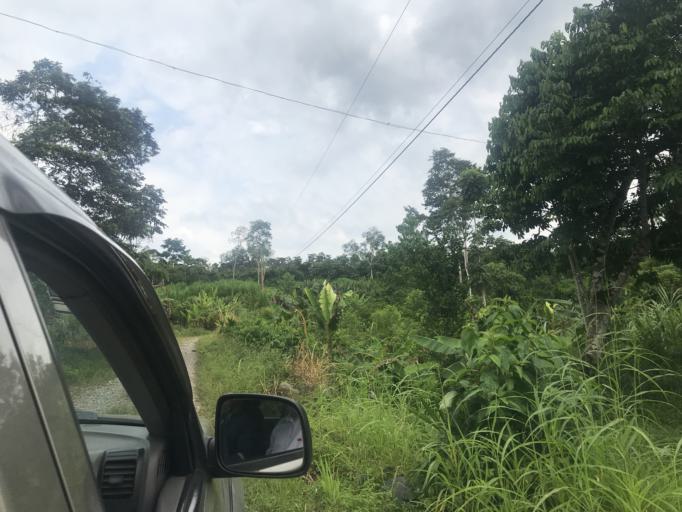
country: EC
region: Napo
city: Tena
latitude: -1.0260
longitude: -77.7423
